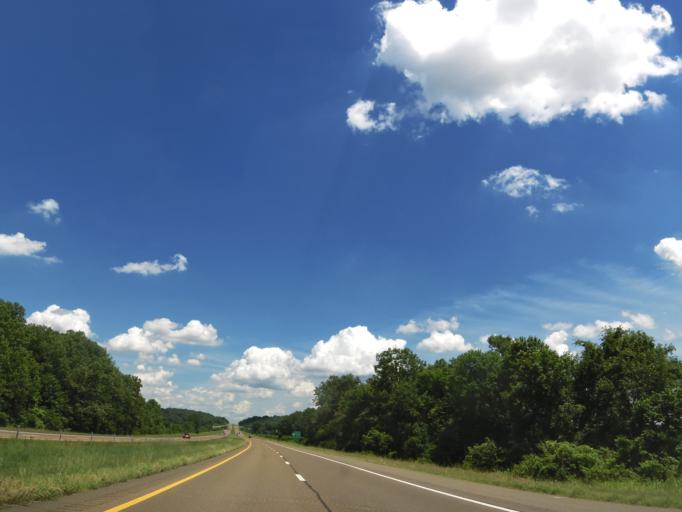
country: US
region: Tennessee
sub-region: Dyer County
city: Dyersburg
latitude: 36.0778
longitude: -89.5158
